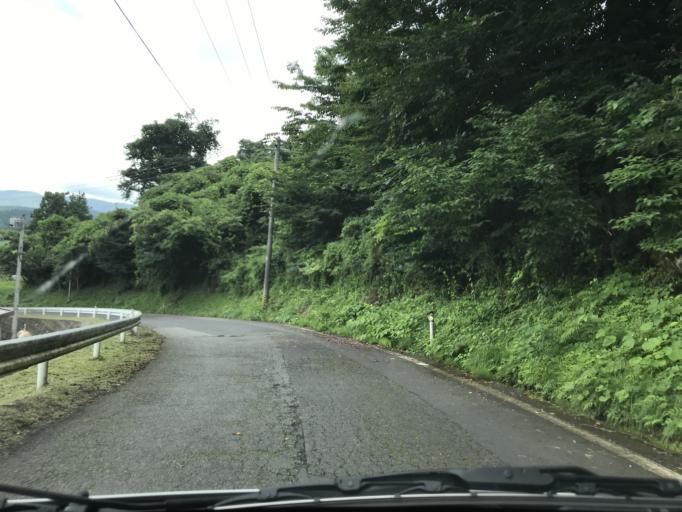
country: JP
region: Iwate
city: Mizusawa
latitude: 39.0403
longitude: 141.3541
